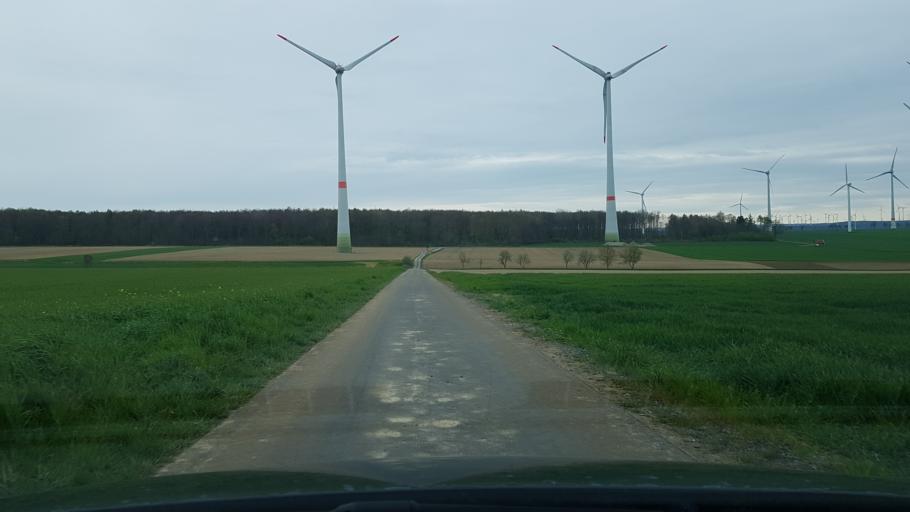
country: DE
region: North Rhine-Westphalia
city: Lichtenau
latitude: 51.6317
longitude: 8.8164
